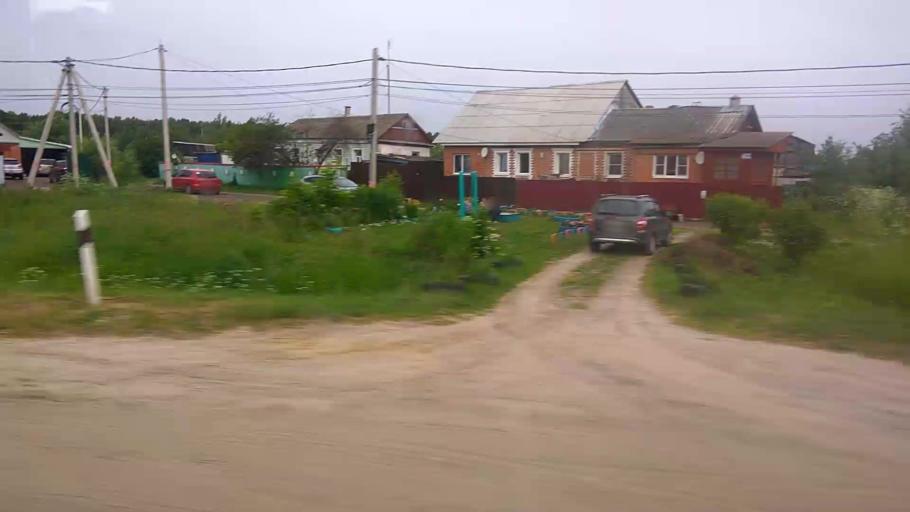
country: RU
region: Moskovskaya
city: Lukhovitsy
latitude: 54.9331
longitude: 39.0043
